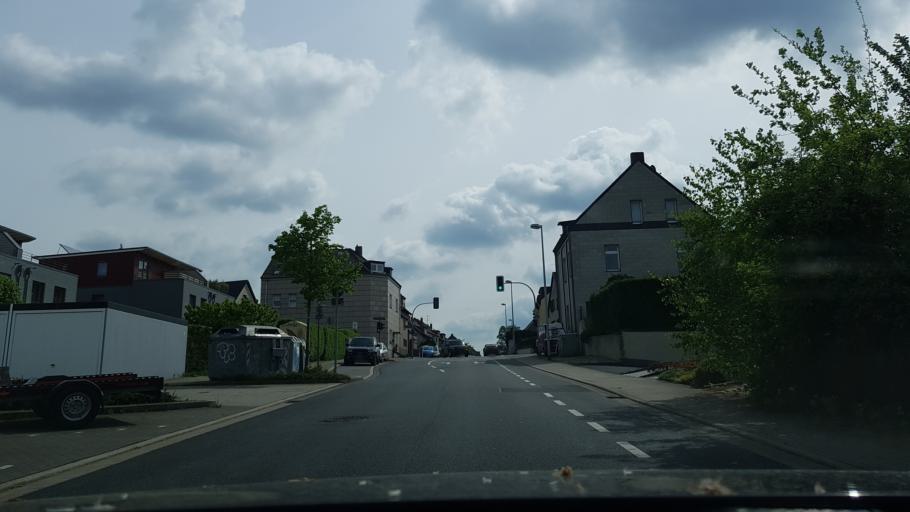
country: DE
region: North Rhine-Westphalia
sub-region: Regierungsbezirk Dusseldorf
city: Muelheim (Ruhr)
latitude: 51.4295
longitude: 6.9050
